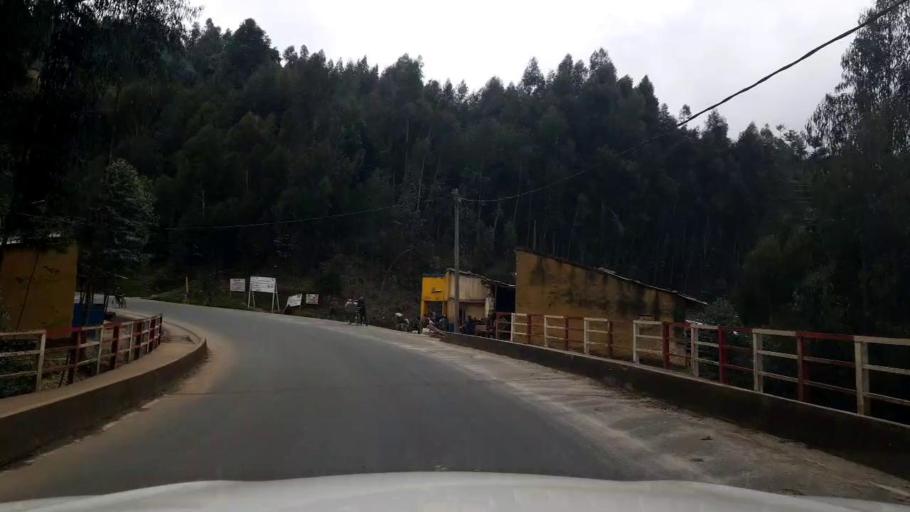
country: RW
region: Northern Province
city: Musanze
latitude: -1.6512
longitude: 29.5077
